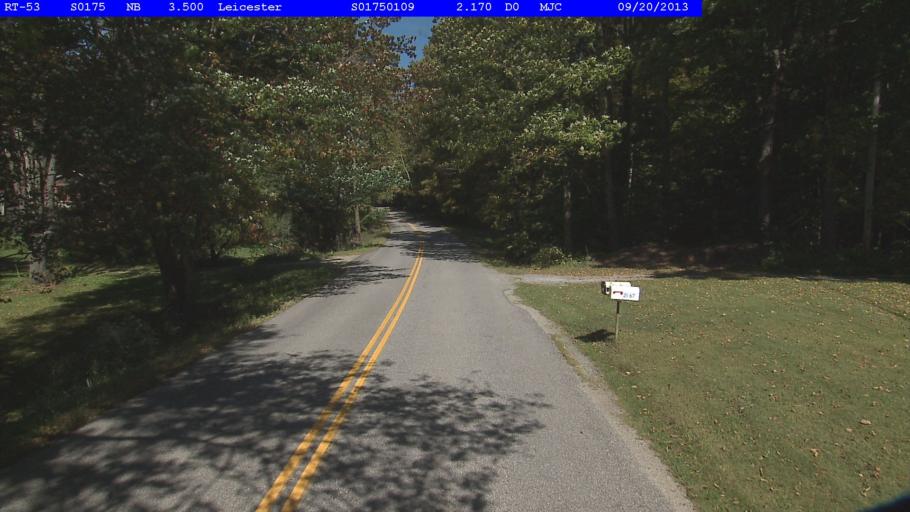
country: US
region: Vermont
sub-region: Rutland County
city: Brandon
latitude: 43.8741
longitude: -73.0640
